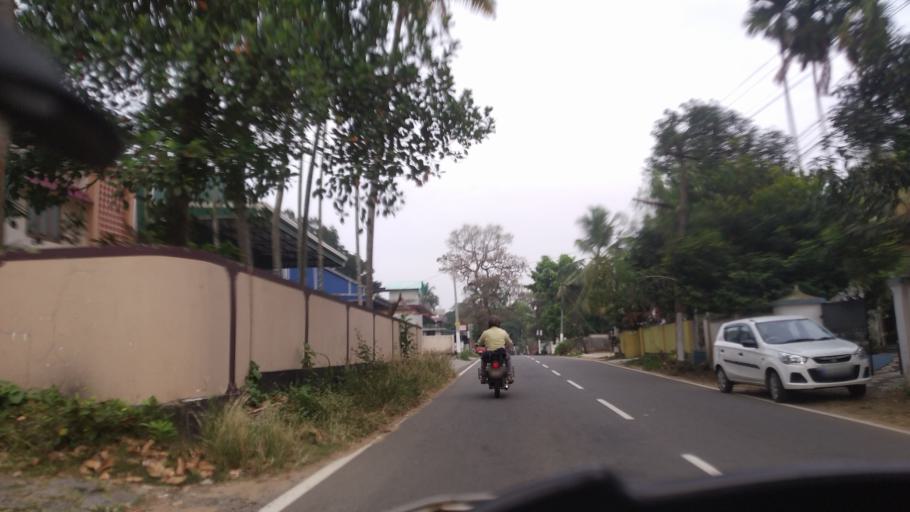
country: IN
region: Kerala
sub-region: Ernakulam
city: Elur
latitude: 10.1492
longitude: 76.2529
